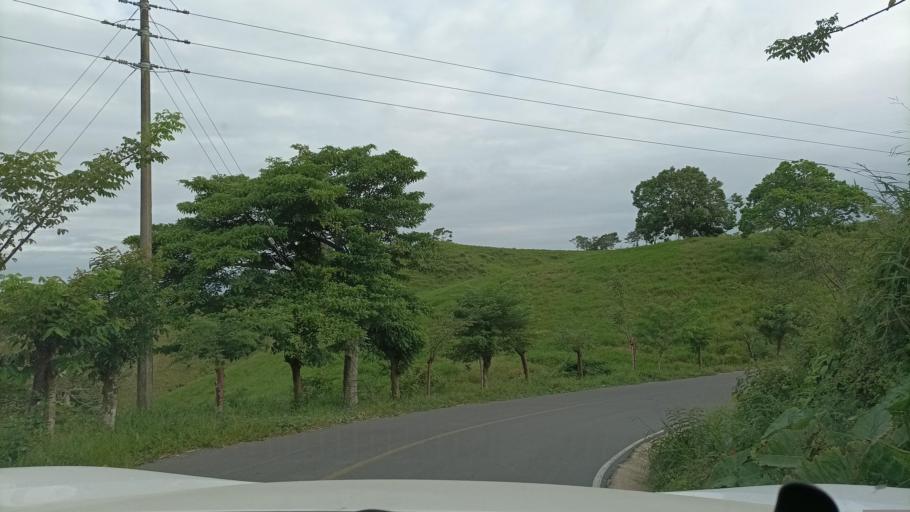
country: MX
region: Veracruz
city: Hidalgotitlan
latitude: 17.6875
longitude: -94.4650
